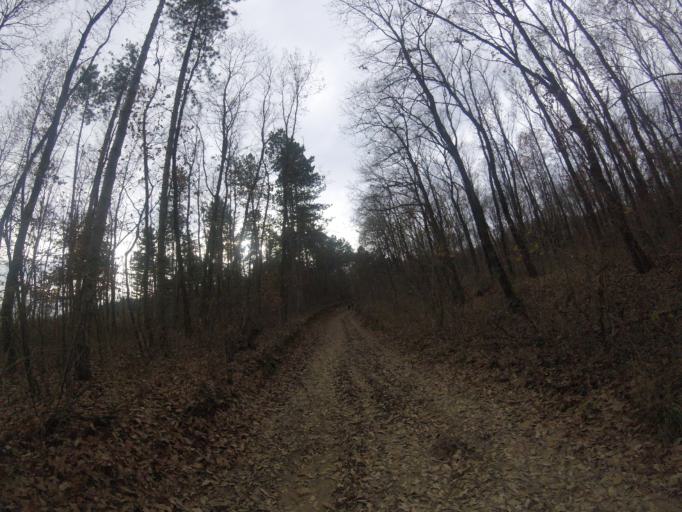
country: HU
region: Tolna
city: Bonyhad
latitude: 46.2616
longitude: 18.6348
